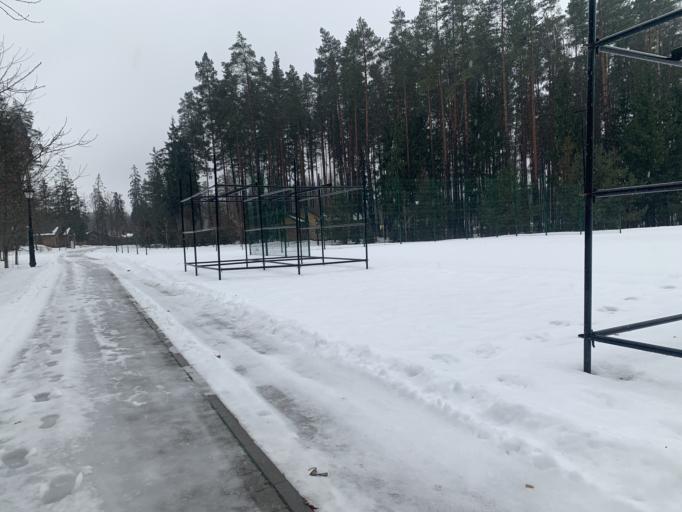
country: BY
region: Minsk
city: Slabada
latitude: 53.9493
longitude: 27.9833
